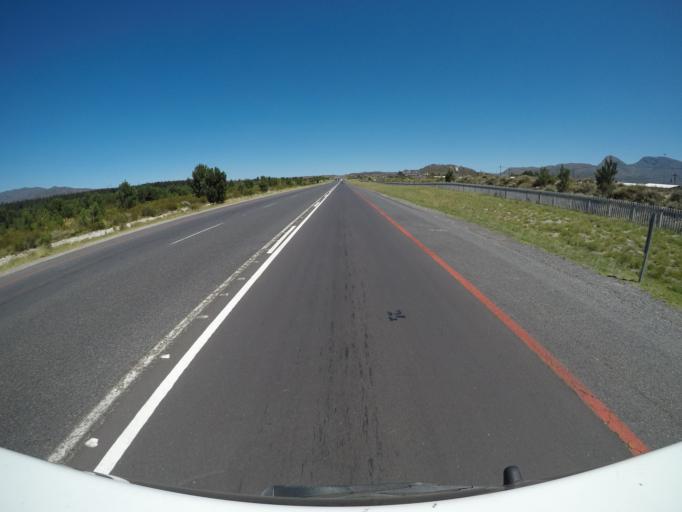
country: ZA
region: Western Cape
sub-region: Overberg District Municipality
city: Grabouw
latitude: -34.1652
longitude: 18.9940
